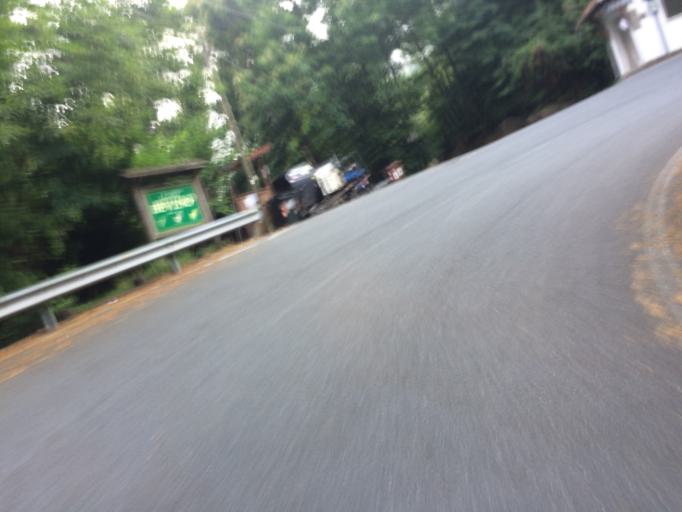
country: IT
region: Liguria
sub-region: Provincia di Imperia
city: Seborga
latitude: 43.8510
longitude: 7.7205
